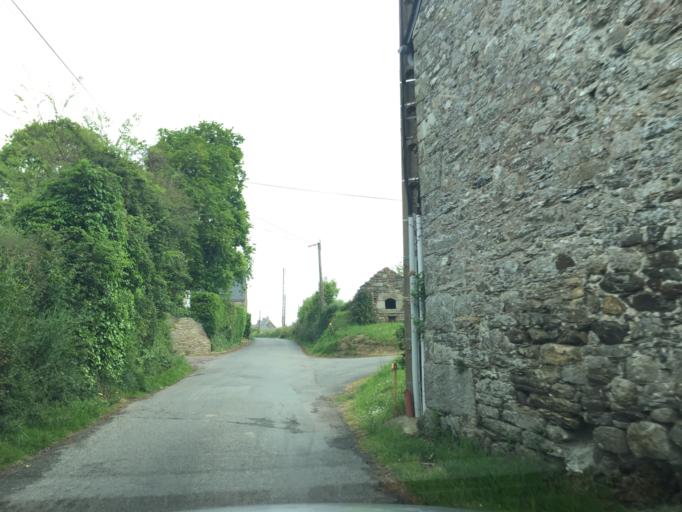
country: FR
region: Brittany
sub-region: Departement des Cotes-d'Armor
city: Saint-Cast-le-Guildo
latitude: 48.5960
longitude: -2.2341
